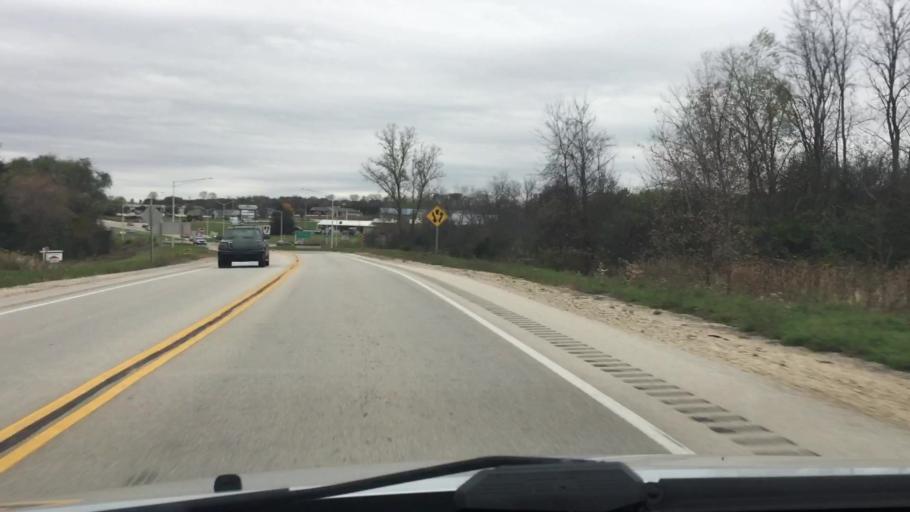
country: US
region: Wisconsin
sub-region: Waukesha County
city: Wales
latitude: 42.9588
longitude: -88.3575
